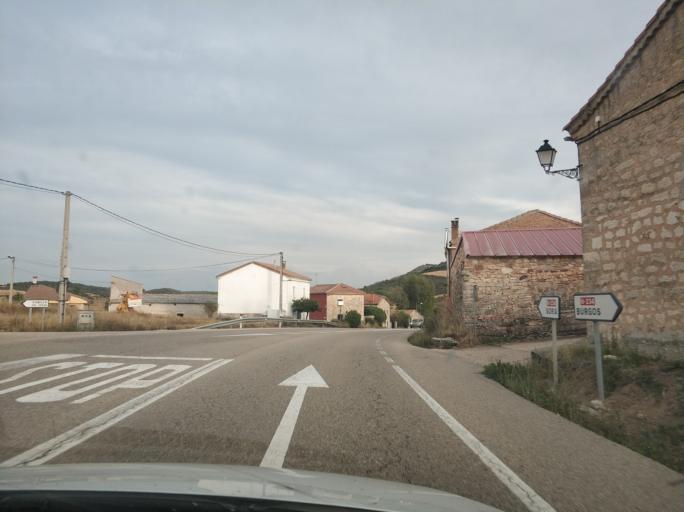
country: ES
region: Castille and Leon
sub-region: Provincia de Burgos
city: Cuevas de San Clemente
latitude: 42.1308
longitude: -3.5681
